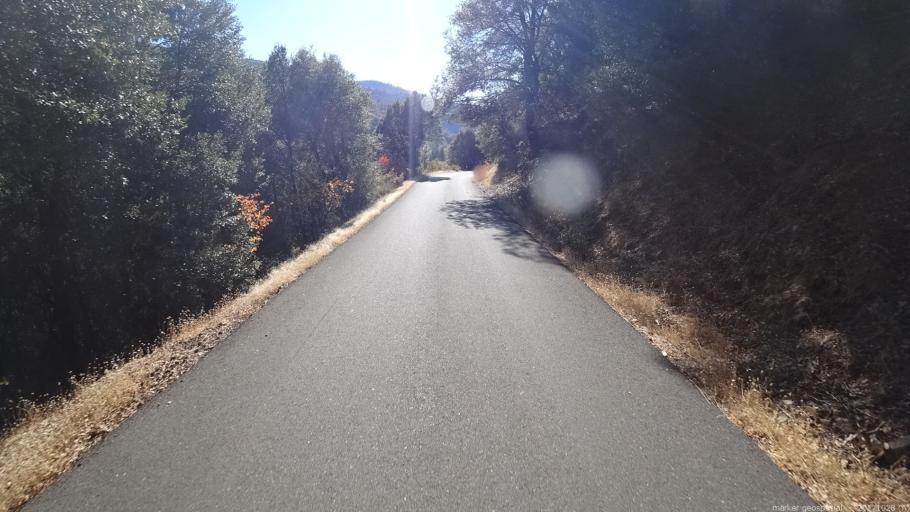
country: US
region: California
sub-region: Trinity County
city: Lewiston
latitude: 40.8008
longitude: -122.6129
